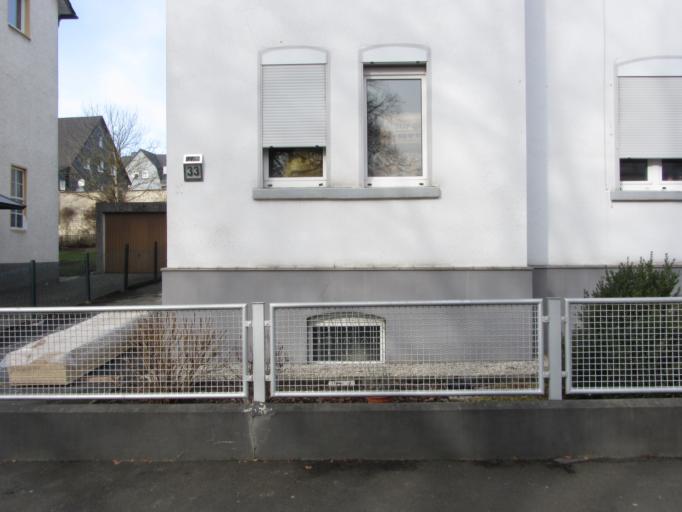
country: DE
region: North Rhine-Westphalia
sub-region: Regierungsbezirk Arnsberg
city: Siegen
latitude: 50.8822
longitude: 8.0222
